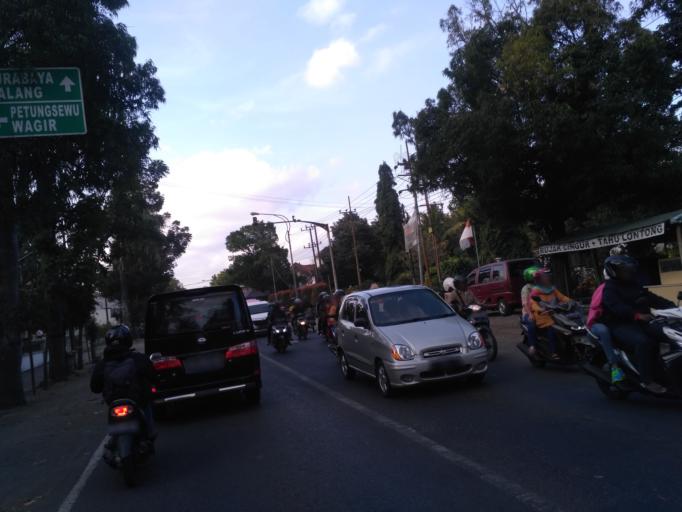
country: ID
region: East Java
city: Kebonsari
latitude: -8.0283
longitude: 112.6155
